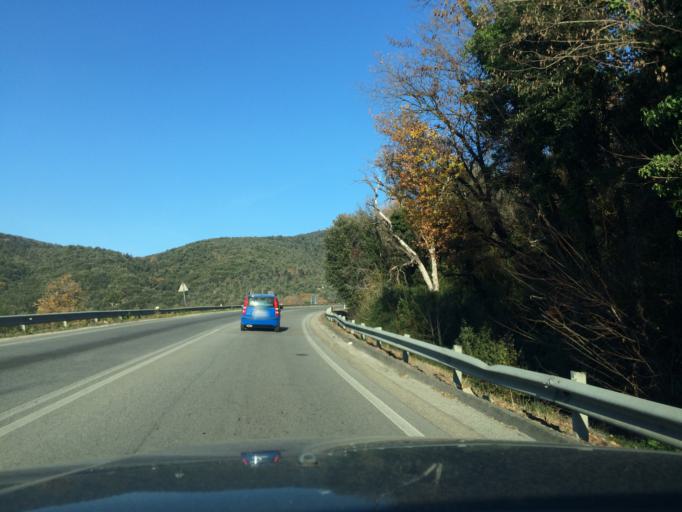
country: IT
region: Umbria
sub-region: Provincia di Terni
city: Fornole
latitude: 42.5353
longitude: 12.4756
